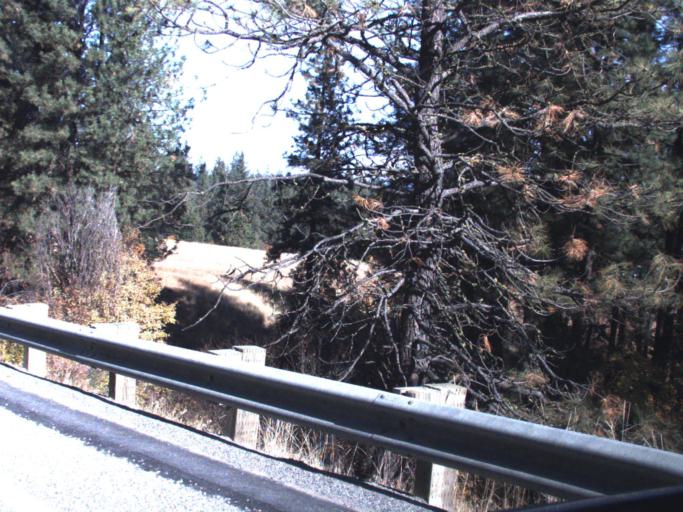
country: US
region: Washington
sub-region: Stevens County
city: Kettle Falls
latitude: 48.6071
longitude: -118.1384
